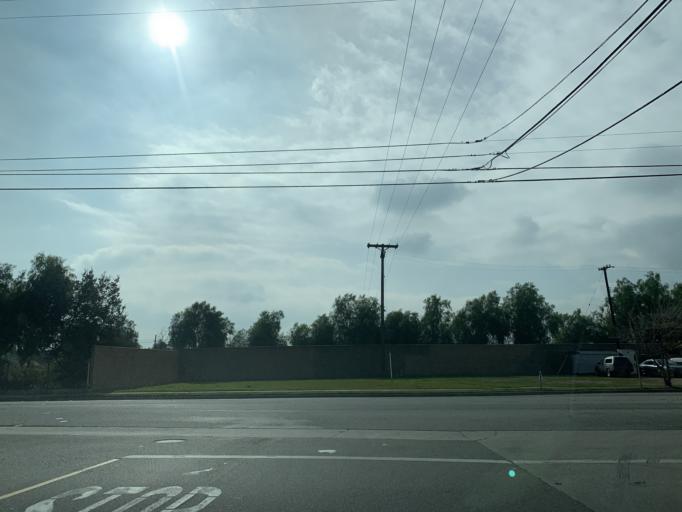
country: US
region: California
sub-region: Los Angeles County
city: Citrus
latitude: 34.1218
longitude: -117.9025
